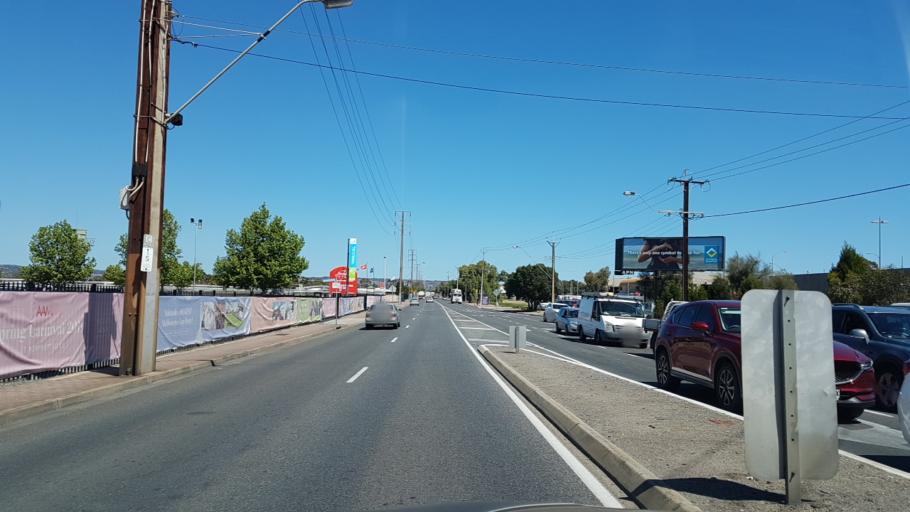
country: AU
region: South Australia
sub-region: Holdfast Bay
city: Glenelg East
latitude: -34.9761
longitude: 138.5379
